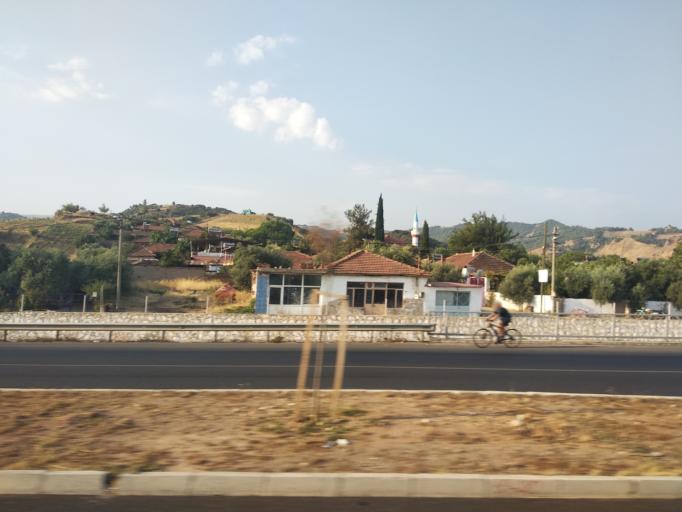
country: TR
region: Manisa
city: Ahmetli
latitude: 38.5094
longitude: 27.9804
